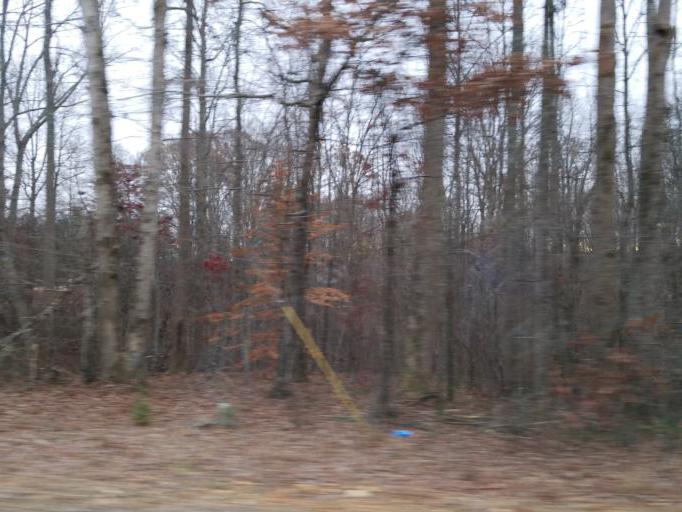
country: US
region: Georgia
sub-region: Dawson County
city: Dawsonville
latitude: 34.4242
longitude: -84.0478
